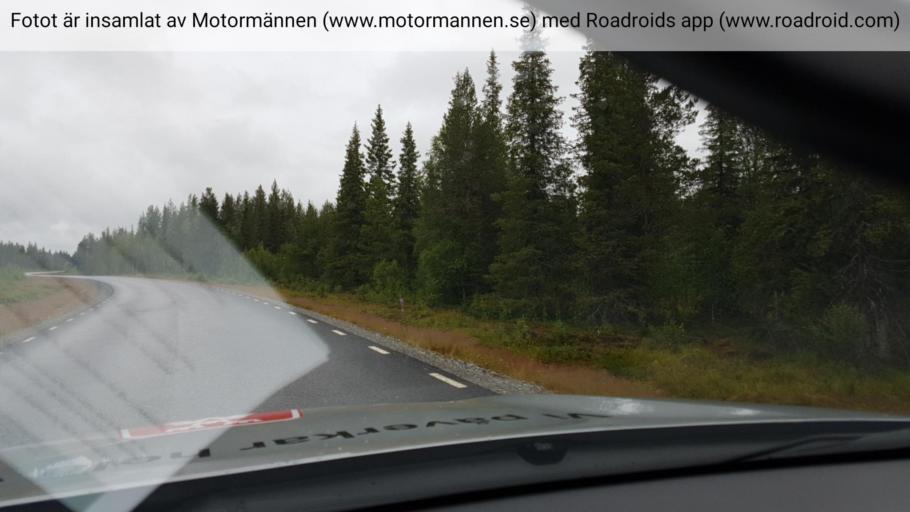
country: SE
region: Norrbotten
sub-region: Gallivare Kommun
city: Gaellivare
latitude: 66.8122
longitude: 21.0444
